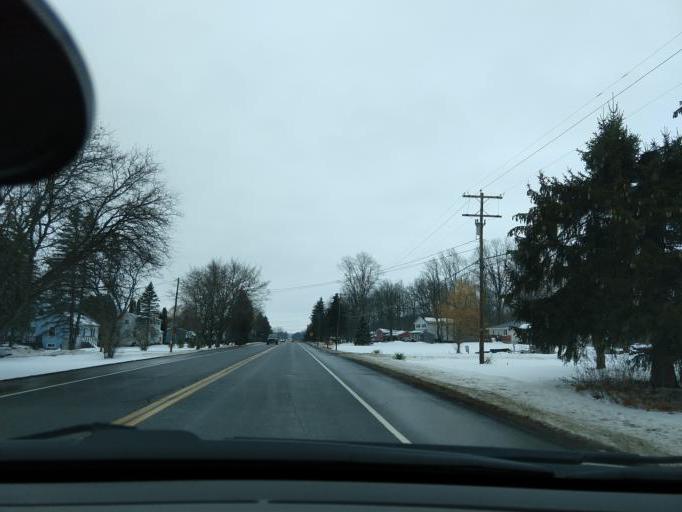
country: US
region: New York
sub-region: Tompkins County
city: Lansing
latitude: 42.5331
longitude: -76.4922
